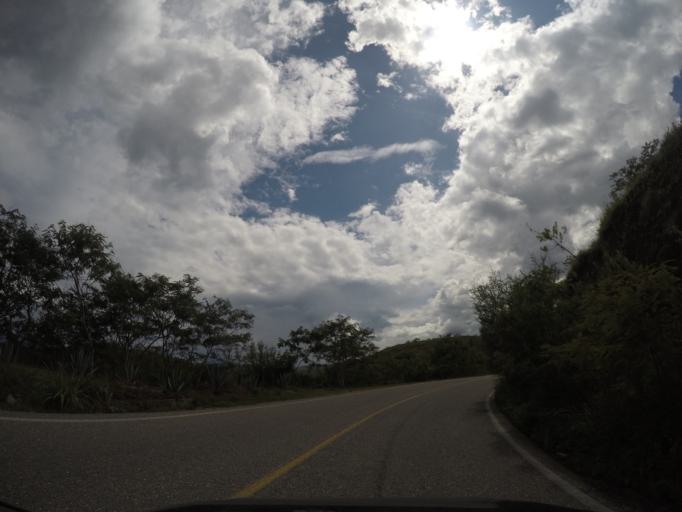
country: MX
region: Oaxaca
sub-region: San Jeronimo Coatlan
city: San Cristobal Honduras
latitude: 16.4301
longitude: -97.0678
